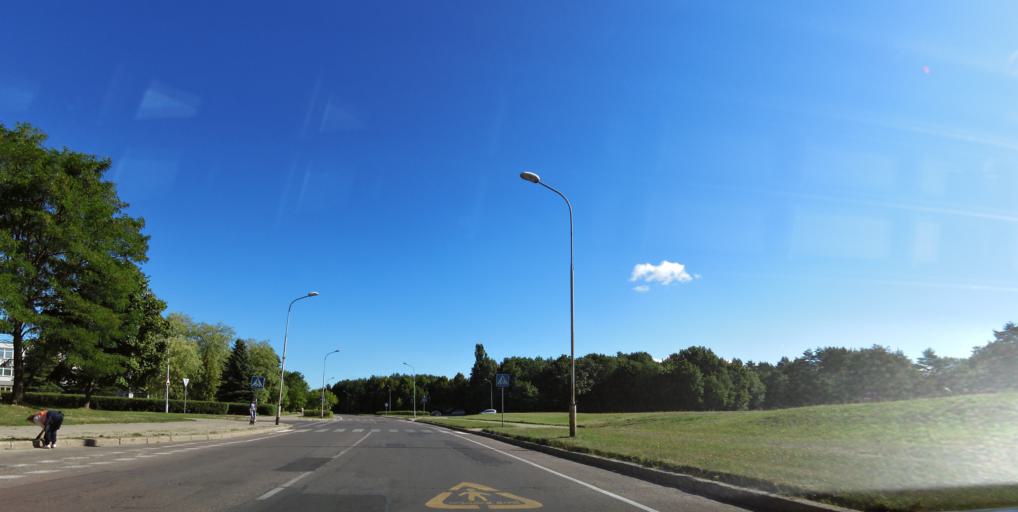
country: LT
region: Vilnius County
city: Justiniskes
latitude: 54.6957
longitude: 25.2278
